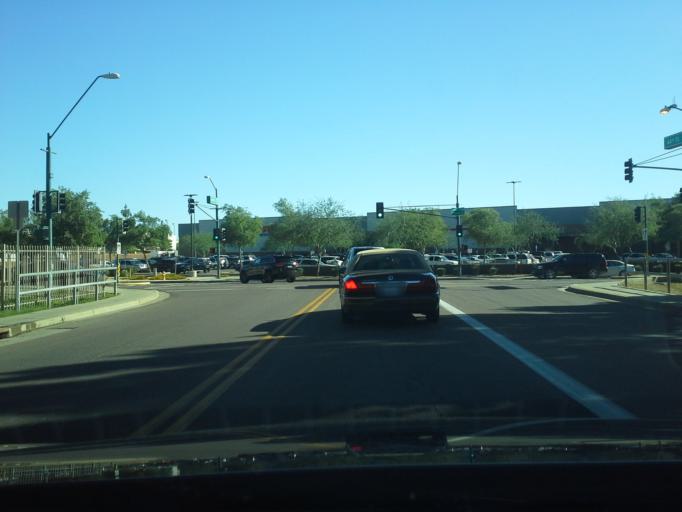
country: US
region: Arizona
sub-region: Maricopa County
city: Paradise Valley
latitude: 33.6052
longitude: -111.9863
